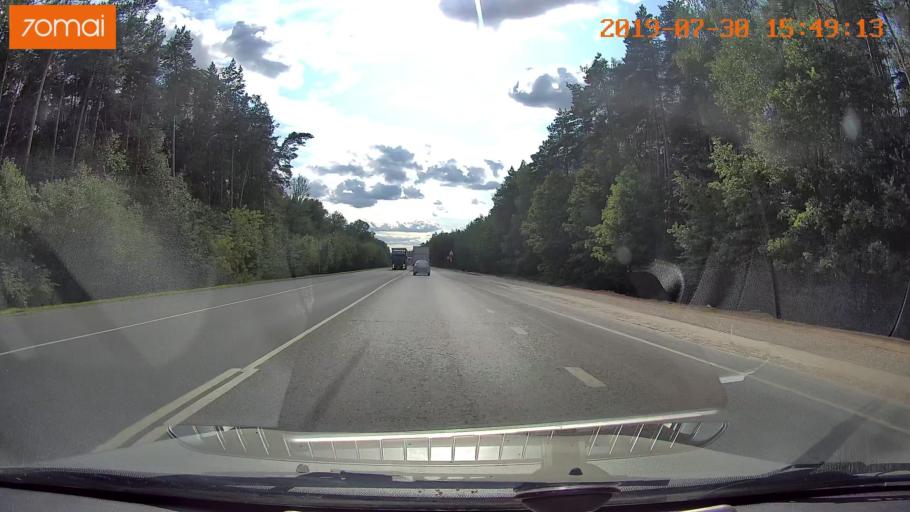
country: RU
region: Moskovskaya
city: Voskresensk
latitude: 55.3387
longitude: 38.6707
